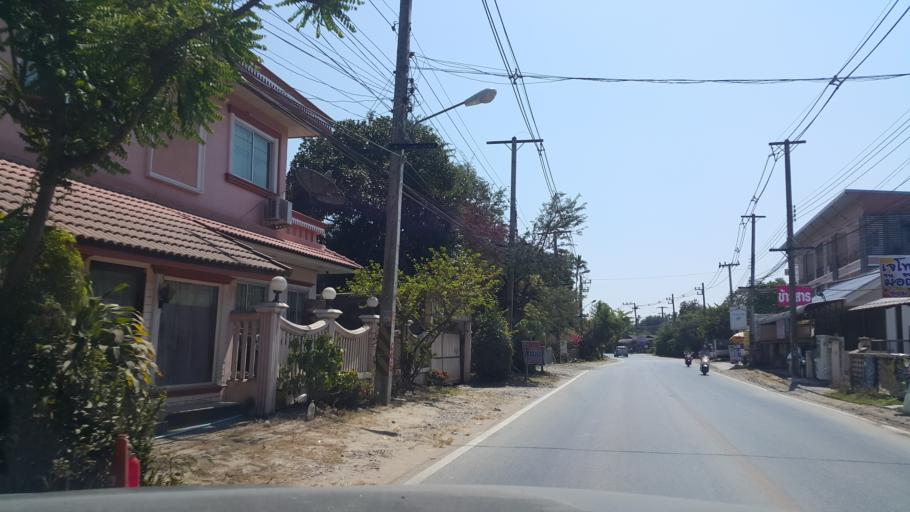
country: TH
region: Chiang Mai
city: San Sai
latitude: 18.8711
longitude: 99.0510
